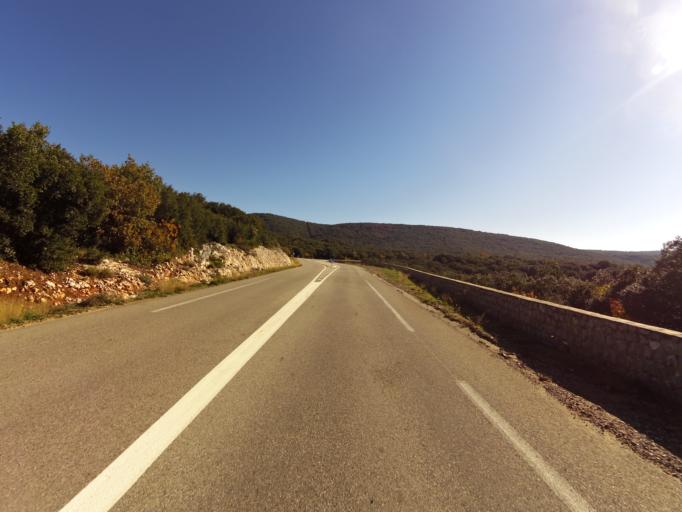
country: FR
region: Rhone-Alpes
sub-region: Departement de l'Ardeche
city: Ruoms
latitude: 44.4061
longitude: 4.4242
